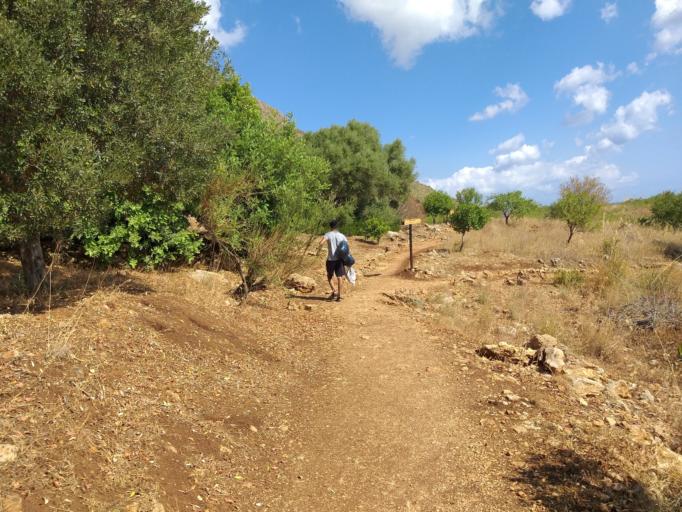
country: IT
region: Sicily
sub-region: Trapani
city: Castelluzzo
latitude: 38.0854
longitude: 12.8064
